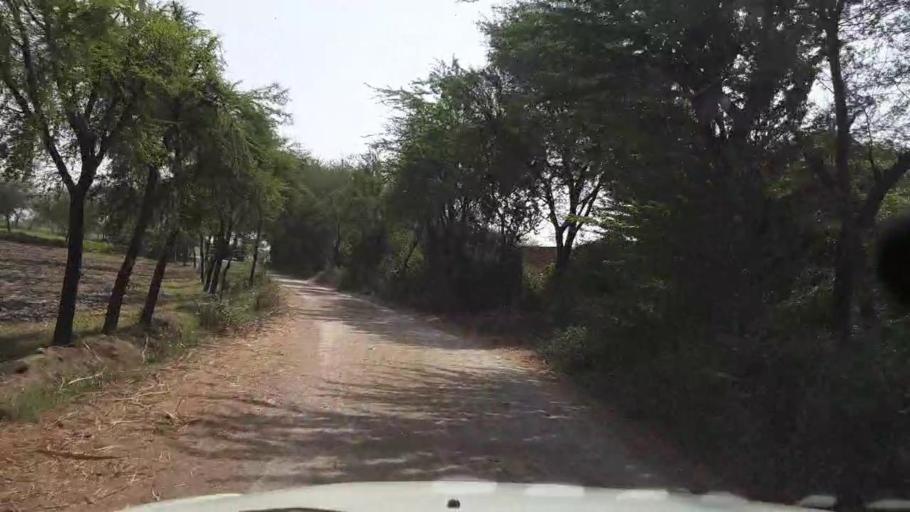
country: PK
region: Sindh
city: Matli
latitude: 25.0262
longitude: 68.7053
